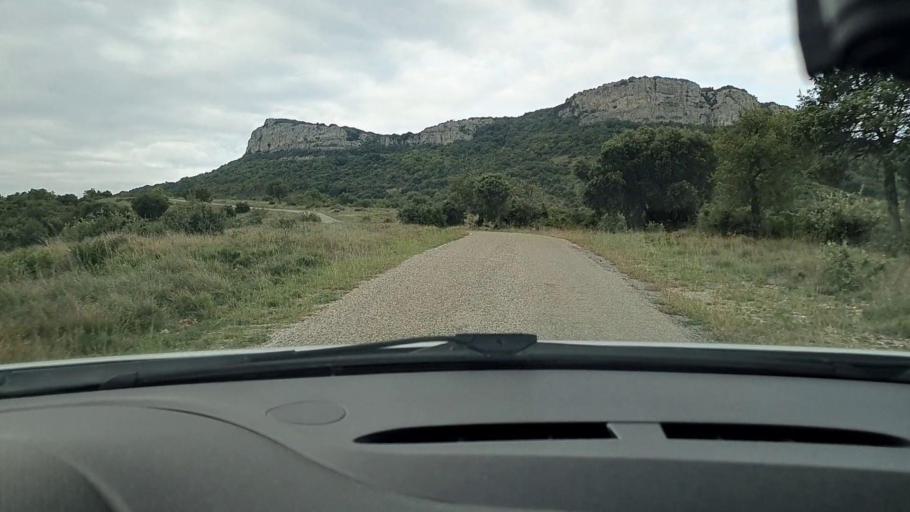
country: FR
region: Languedoc-Roussillon
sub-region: Departement du Gard
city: Mons
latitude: 44.1506
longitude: 4.2915
